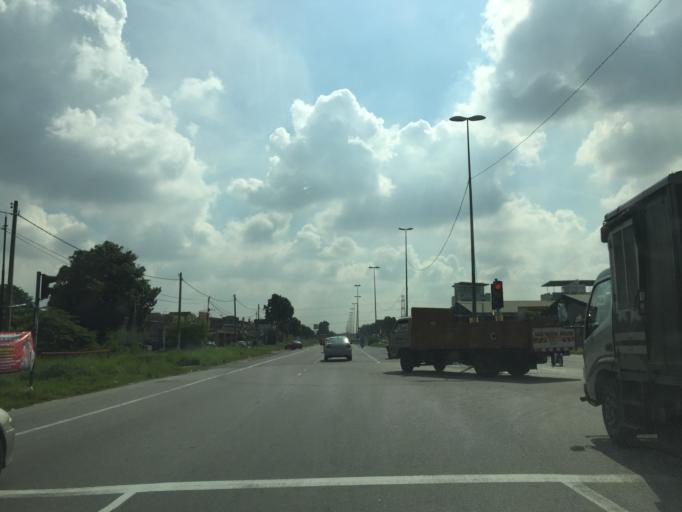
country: MY
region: Selangor
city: Klang
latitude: 3.0143
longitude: 101.4570
